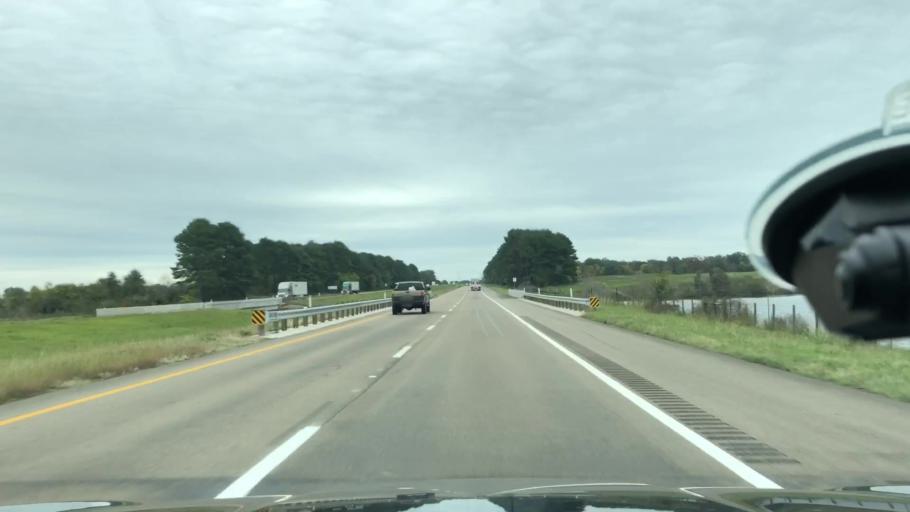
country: US
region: Texas
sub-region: Morris County
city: Omaha
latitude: 33.2923
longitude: -94.7556
